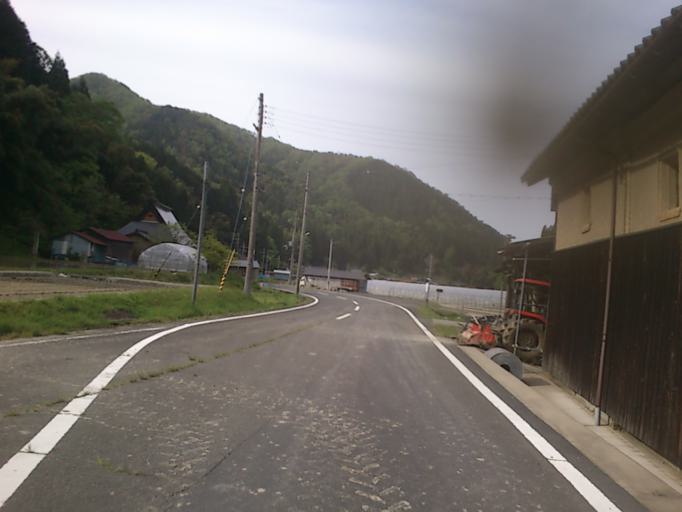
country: JP
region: Kyoto
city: Miyazu
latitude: 35.6105
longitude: 135.0033
